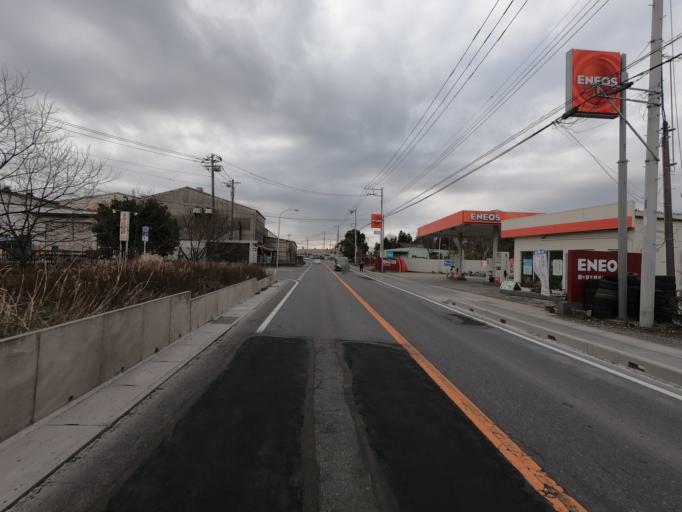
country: JP
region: Ibaraki
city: Ishioka
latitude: 36.0946
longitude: 140.3410
